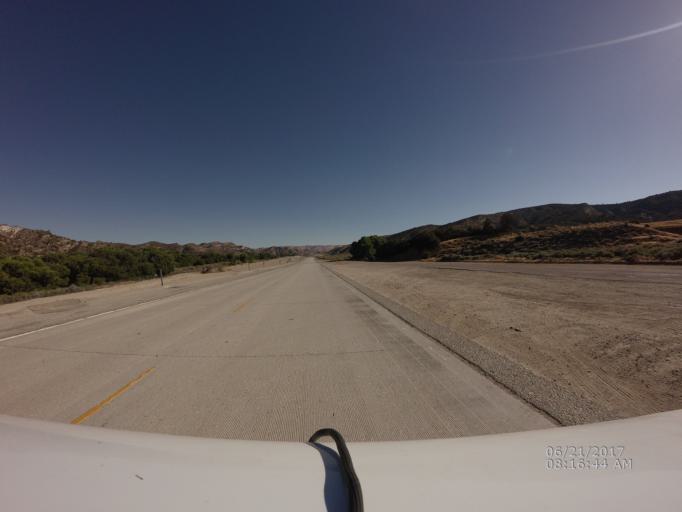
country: US
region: California
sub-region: Kern County
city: Lebec
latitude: 34.7083
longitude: -118.7982
